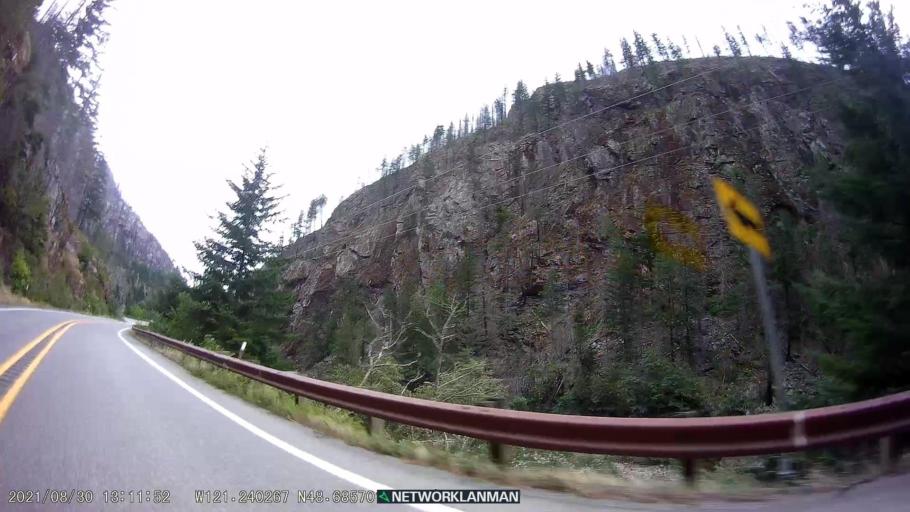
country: US
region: Washington
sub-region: Snohomish County
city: Darrington
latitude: 48.6868
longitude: -121.2412
